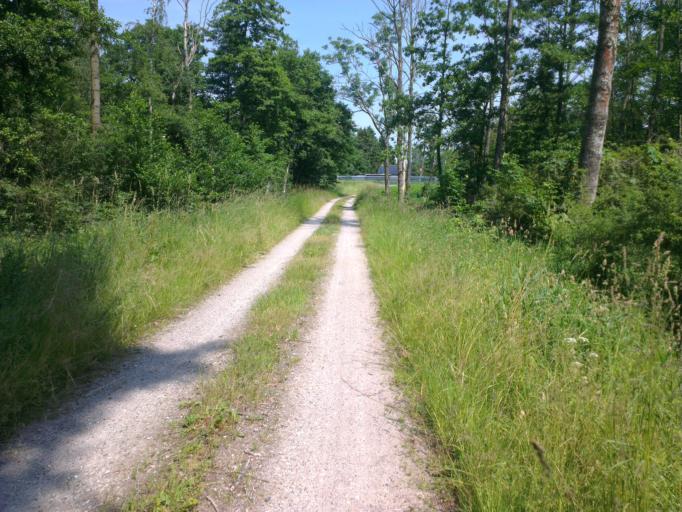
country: DK
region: Capital Region
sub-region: Hillerod Kommune
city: Nodebo
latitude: 55.9314
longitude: 12.3637
